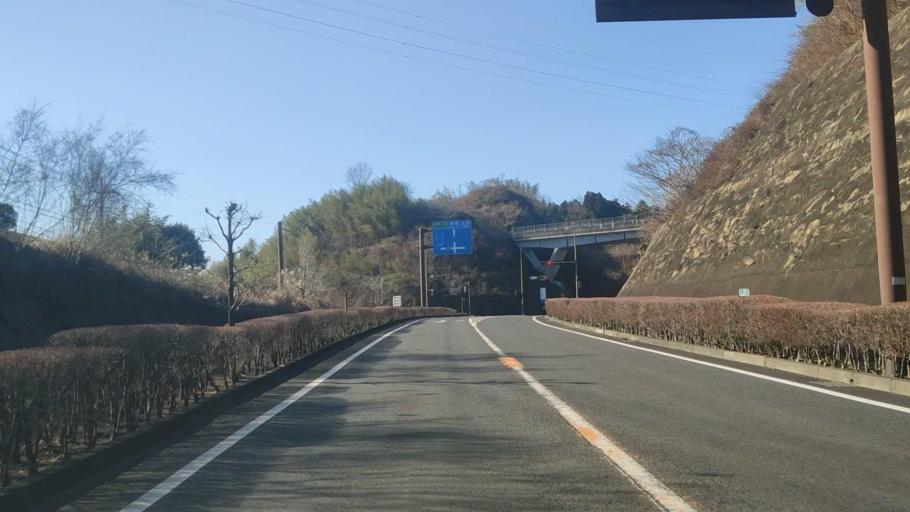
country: JP
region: Oita
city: Oita
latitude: 33.0708
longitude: 131.6325
